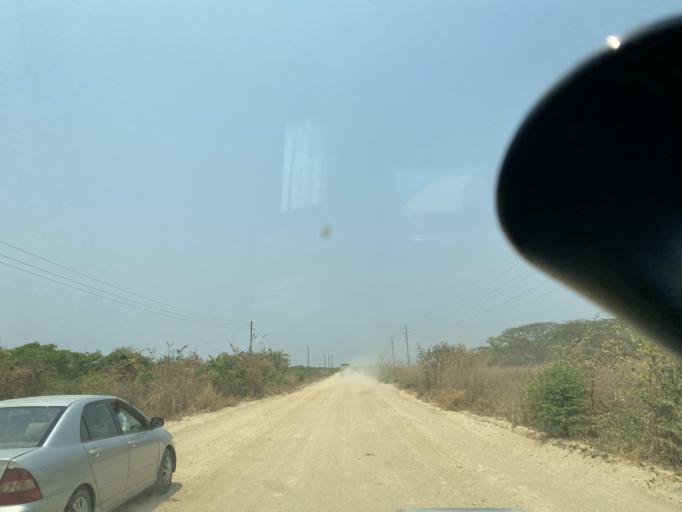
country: ZM
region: Lusaka
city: Lusaka
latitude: -15.5344
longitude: 28.3470
